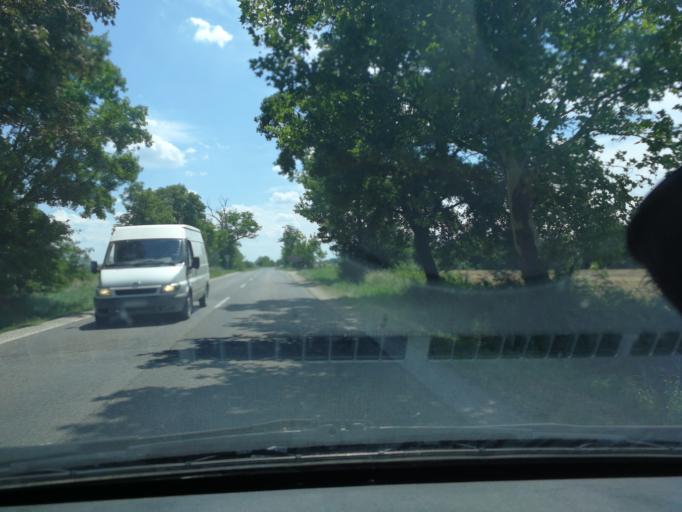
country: HU
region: Bacs-Kiskun
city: Tass
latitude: 47.0549
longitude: 19.0197
